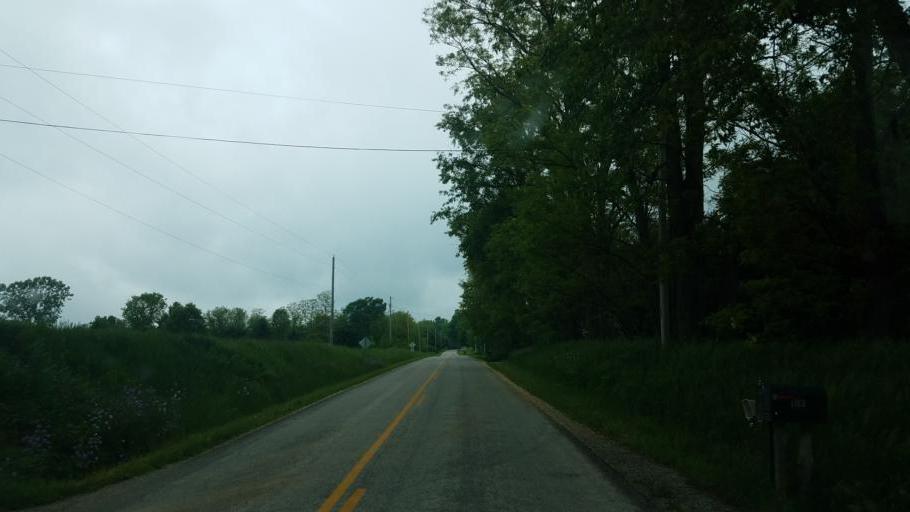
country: US
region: Ohio
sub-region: Ashland County
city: Ashland
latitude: 40.7660
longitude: -82.3499
